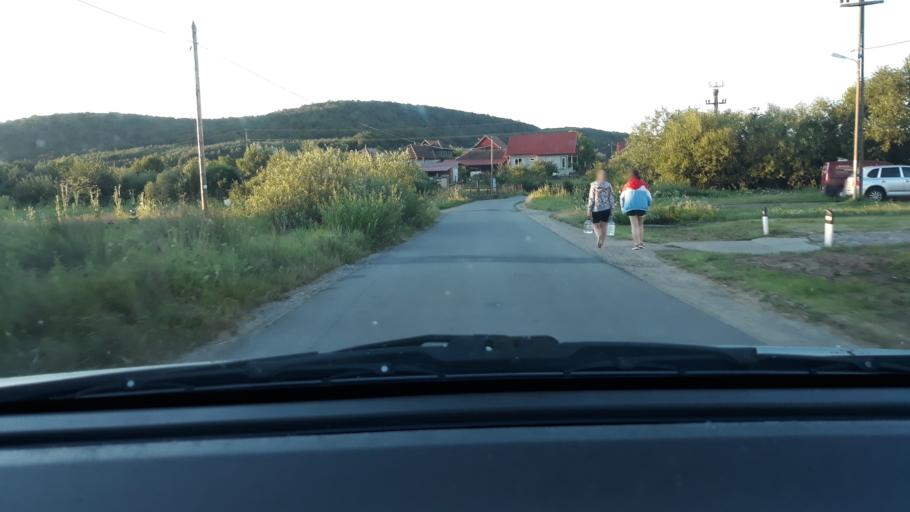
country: RO
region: Bihor
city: Hidiselu de Sus
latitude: 46.9447
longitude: 22.0226
